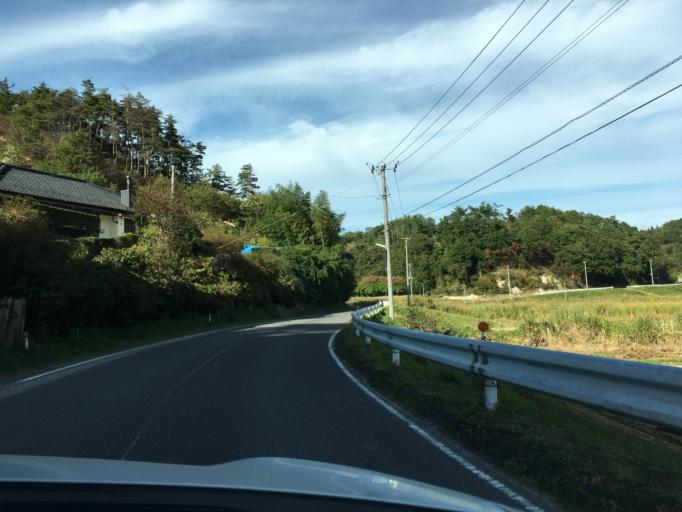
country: JP
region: Fukushima
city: Miharu
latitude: 37.3472
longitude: 140.4720
